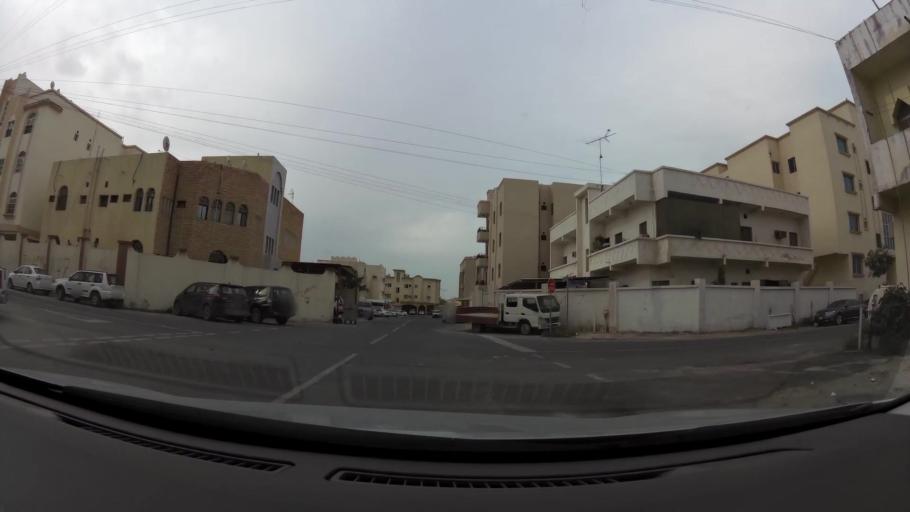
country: QA
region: Baladiyat ad Dawhah
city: Doha
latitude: 25.3056
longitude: 51.4938
